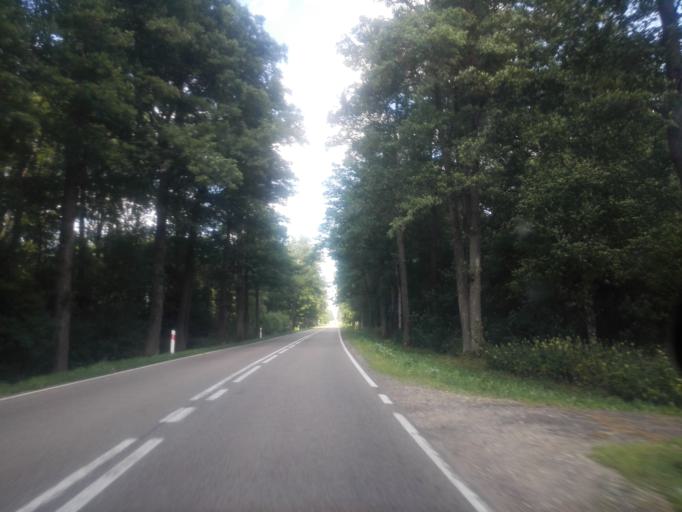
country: PL
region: Podlasie
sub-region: Powiat sejnenski
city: Krasnopol
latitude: 53.9450
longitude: 23.1885
